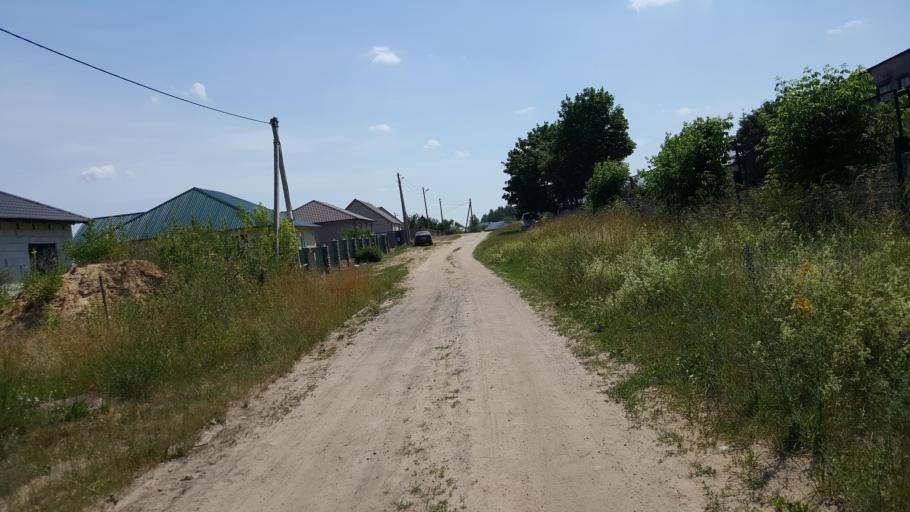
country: BY
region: Brest
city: Kamyanyets
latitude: 52.4047
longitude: 23.8374
